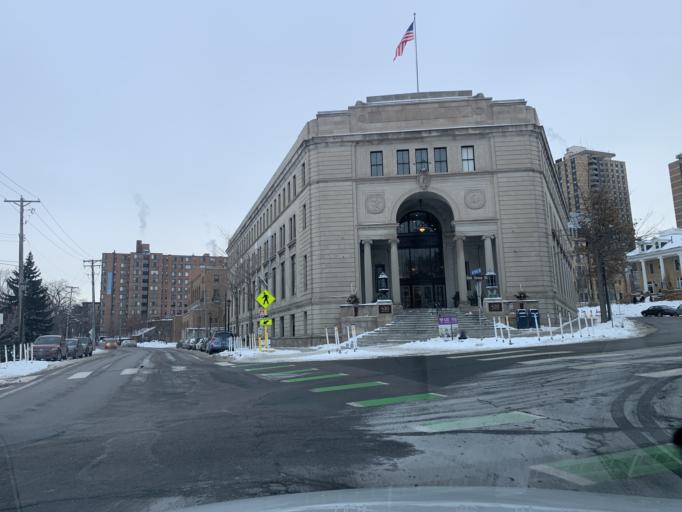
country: US
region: Minnesota
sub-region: Hennepin County
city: Minneapolis
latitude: 44.9685
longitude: -93.2862
